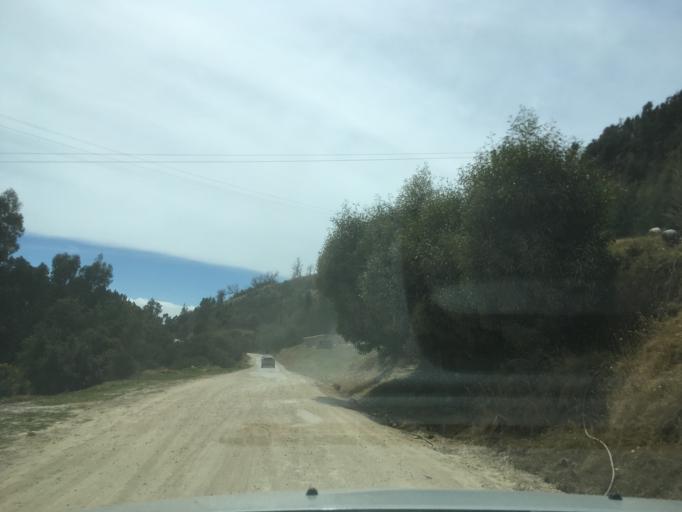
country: CO
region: Boyaca
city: Aquitania
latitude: 5.5908
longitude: -72.9212
